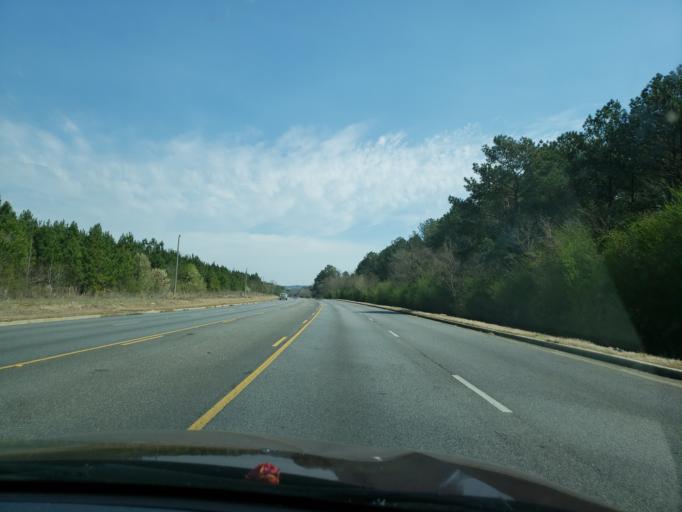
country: US
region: Alabama
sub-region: Elmore County
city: Wetumpka
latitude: 32.5341
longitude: -86.2494
